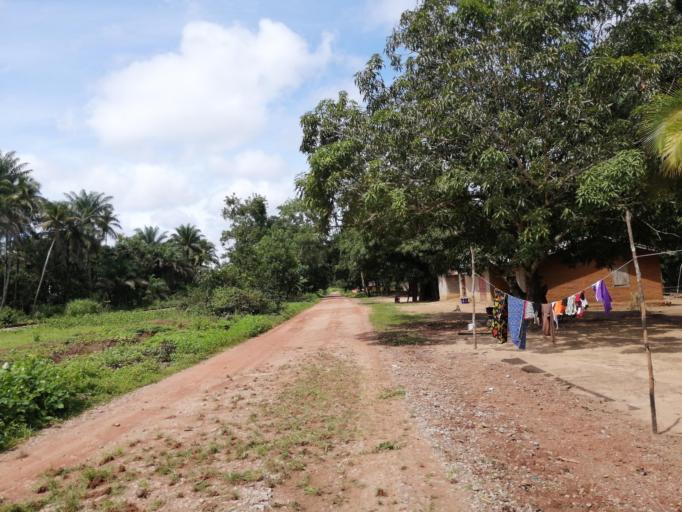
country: SL
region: Northern Province
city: Pepel
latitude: 8.6827
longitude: -12.9993
